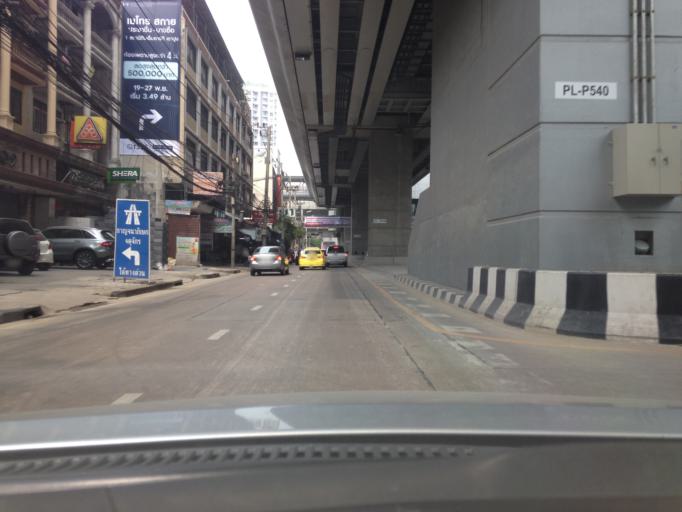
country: TH
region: Bangkok
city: Bang Sue
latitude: 13.8203
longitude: 100.5324
